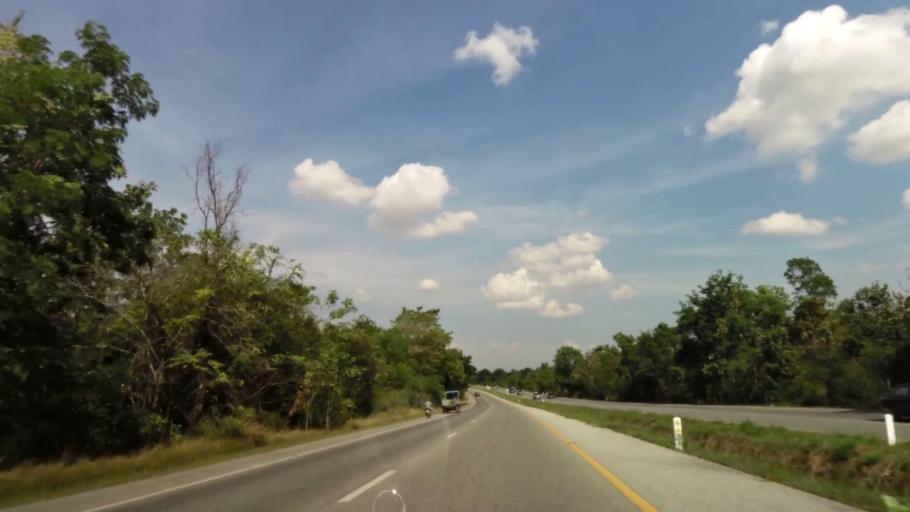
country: TH
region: Uttaradit
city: Thong Saen Khan
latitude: 17.4571
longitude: 100.2378
